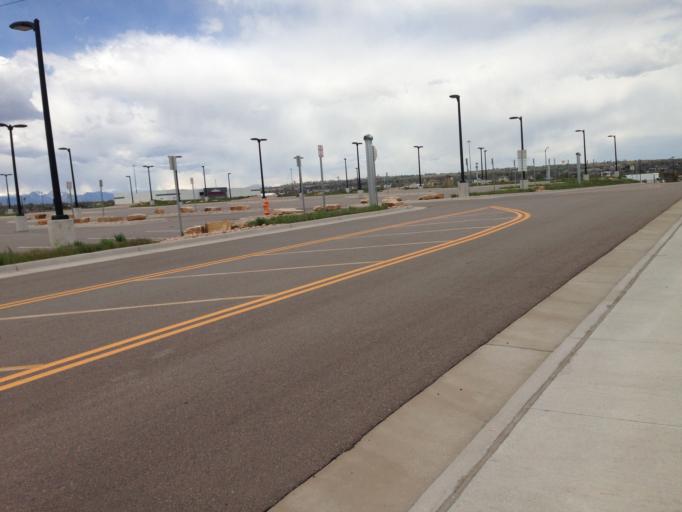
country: US
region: Colorado
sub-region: Adams County
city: Twin Lakes
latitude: 39.8059
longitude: -105.0033
